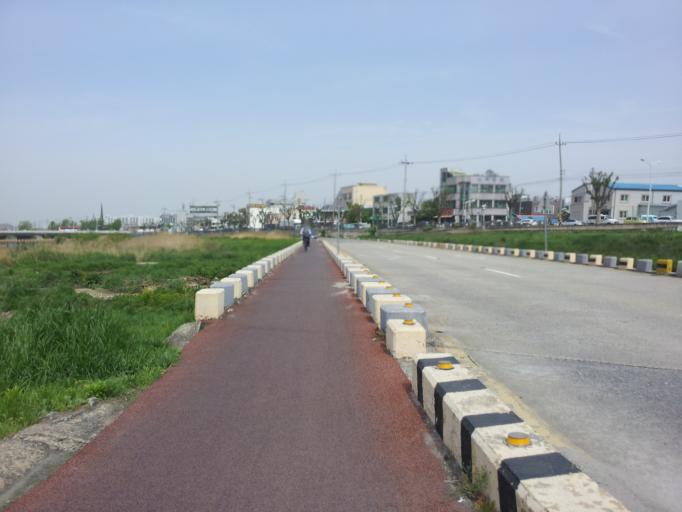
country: KR
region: Daejeon
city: Daejeon
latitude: 36.3369
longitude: 127.4225
